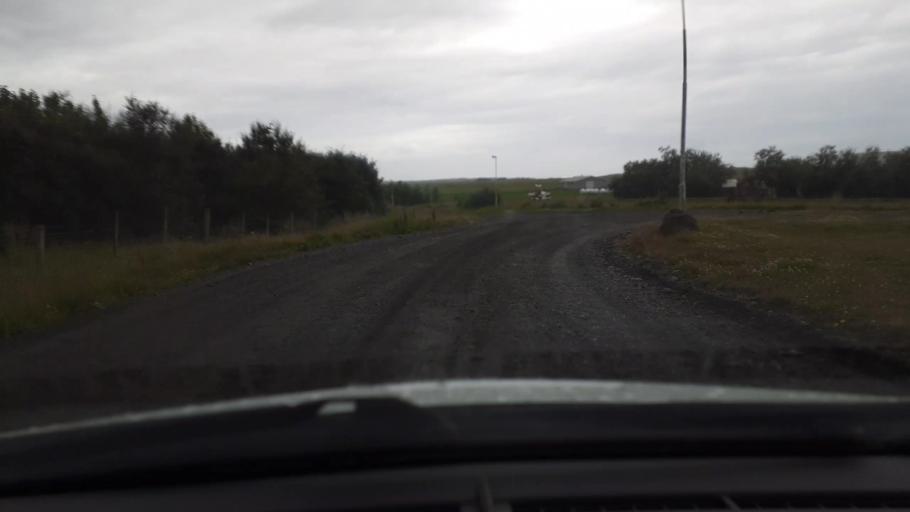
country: IS
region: West
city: Akranes
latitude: 64.3395
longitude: -22.0232
